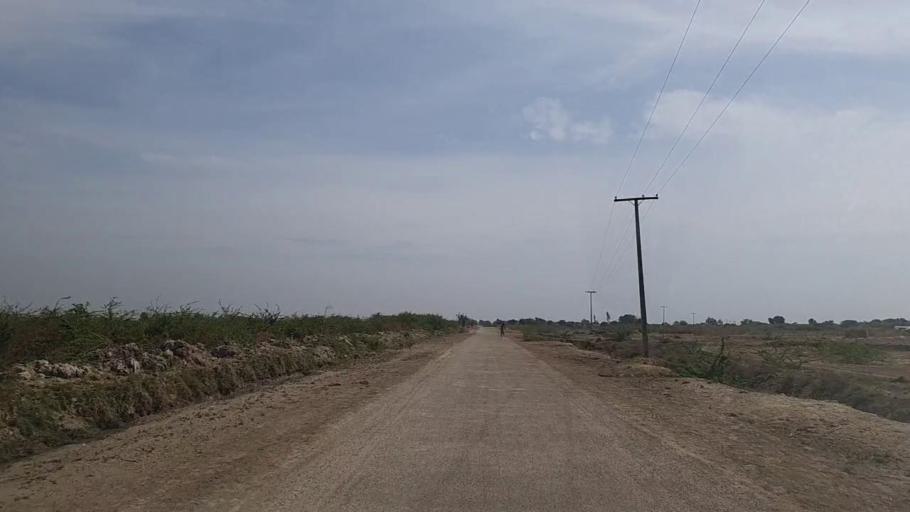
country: PK
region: Sindh
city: Samaro
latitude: 25.2050
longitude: 69.4609
